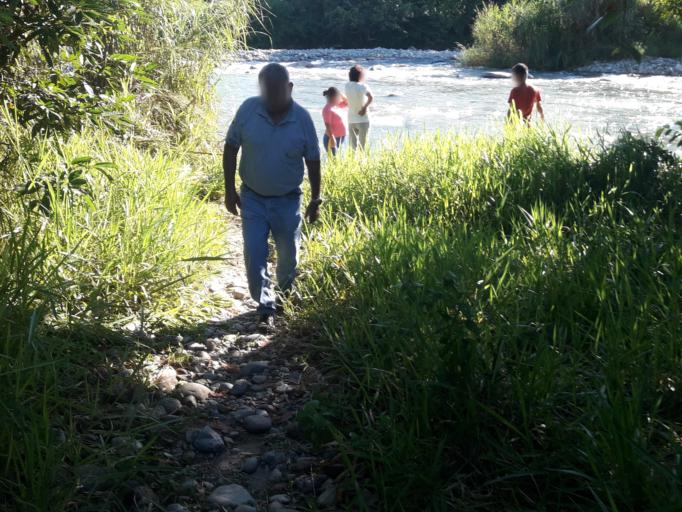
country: EC
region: Napo
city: Tena
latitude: -0.9723
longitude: -77.8568
